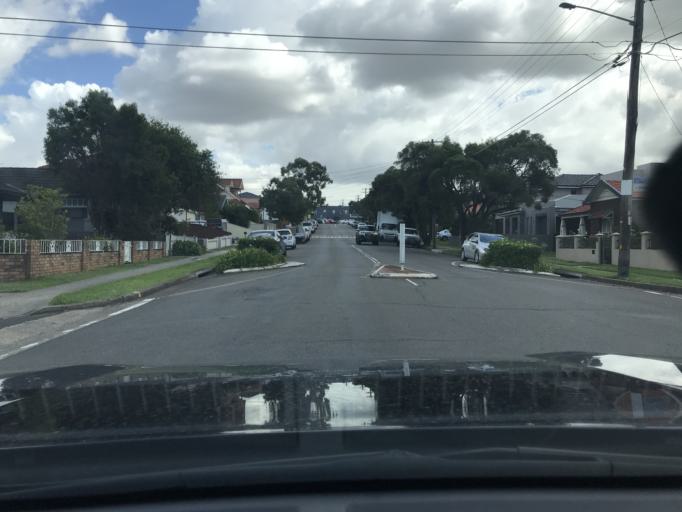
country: AU
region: New South Wales
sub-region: Canada Bay
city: Concord
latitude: -33.8499
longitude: 151.1081
